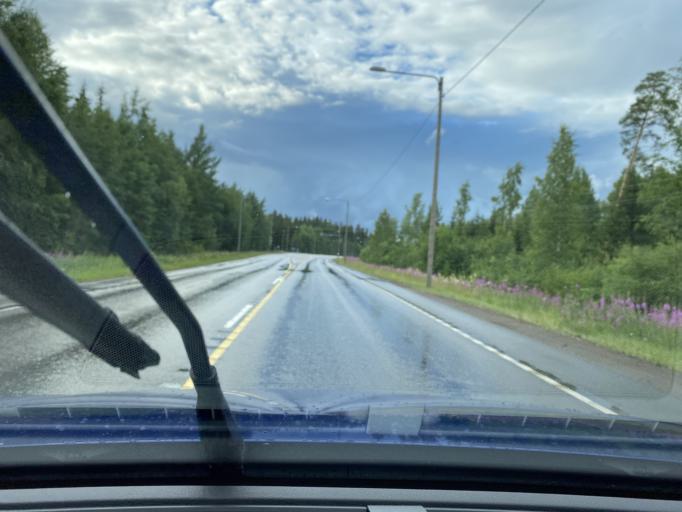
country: FI
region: Uusimaa
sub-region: Helsinki
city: Nurmijaervi
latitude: 60.5141
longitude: 24.8452
